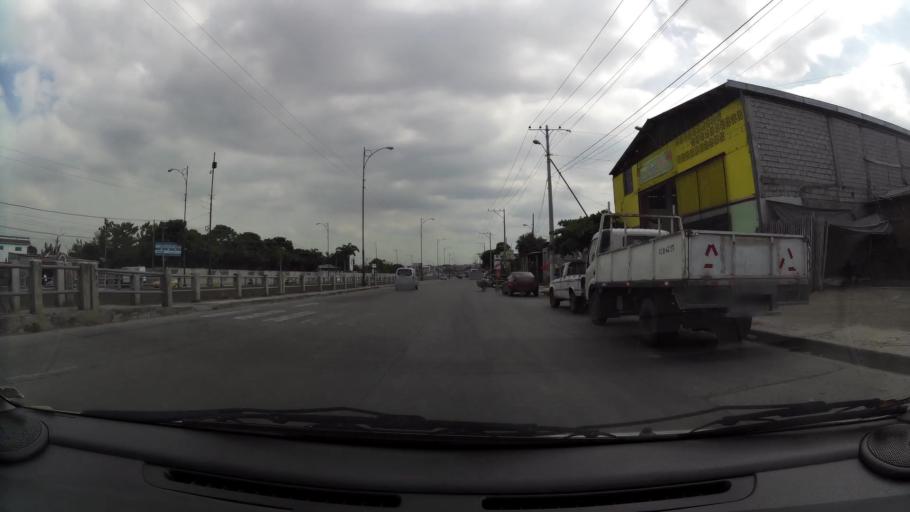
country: EC
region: Guayas
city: Eloy Alfaro
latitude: -2.0885
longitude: -79.9277
